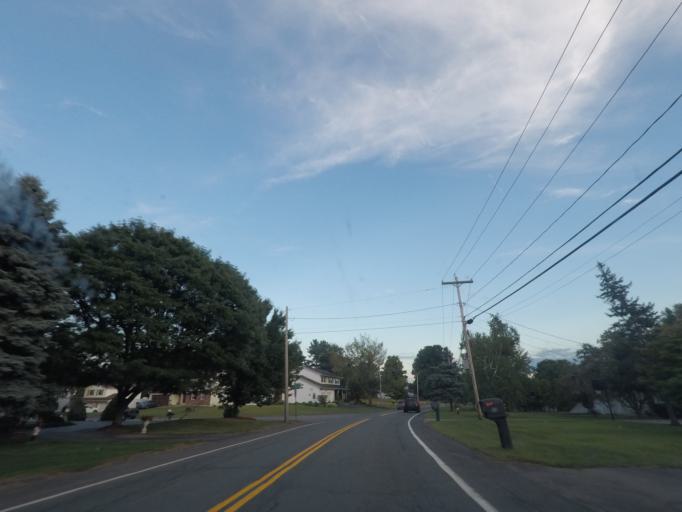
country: US
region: New York
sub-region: Schenectady County
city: Niskayuna
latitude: 42.7762
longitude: -73.7857
